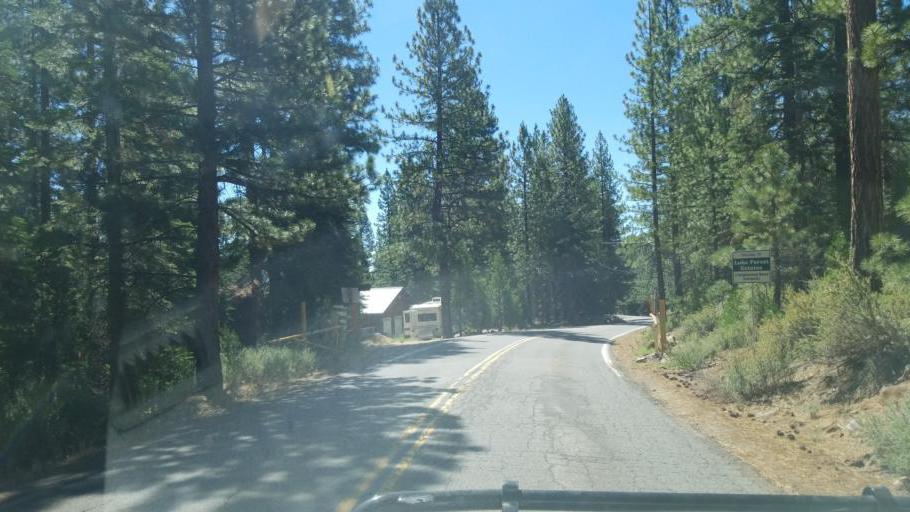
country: US
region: California
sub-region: Lassen County
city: Susanville
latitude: 40.4392
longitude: -120.7472
